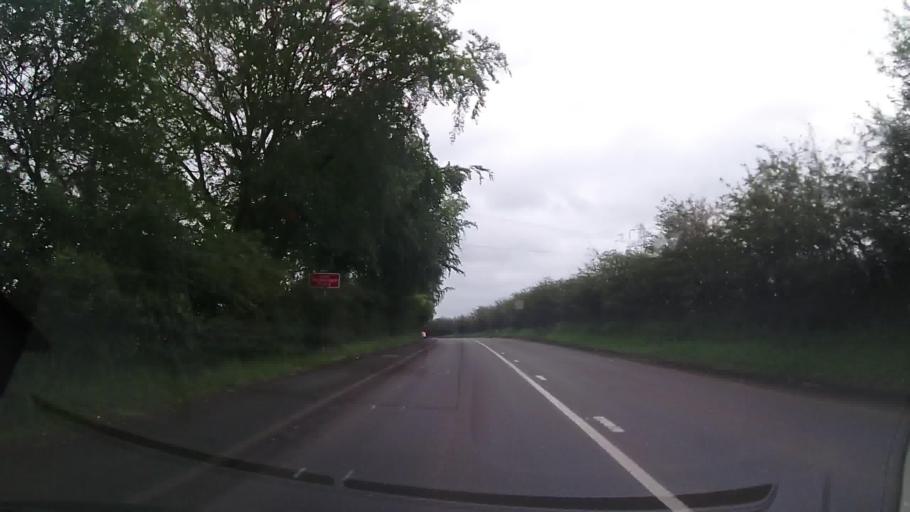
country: GB
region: England
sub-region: Staffordshire
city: Newcastle under Lyme
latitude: 52.9729
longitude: -2.2698
